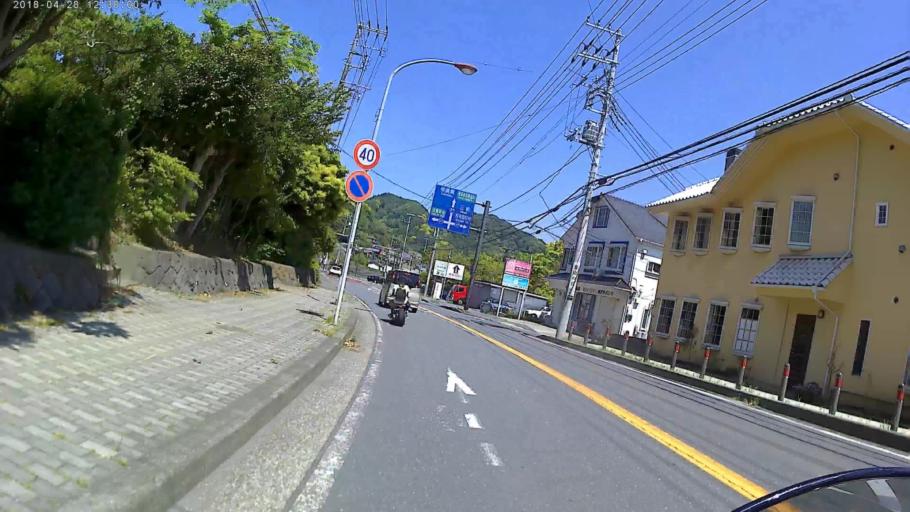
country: JP
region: Kanagawa
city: Hayama
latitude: 35.2669
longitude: 139.6040
